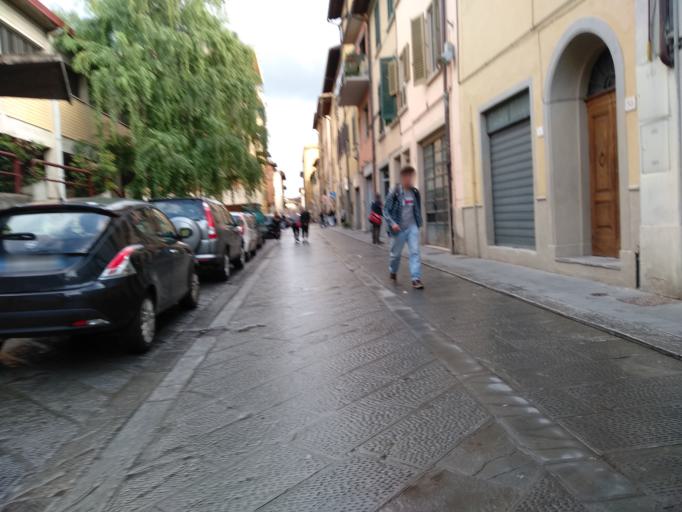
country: IT
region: Tuscany
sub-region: Province of Arezzo
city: San Giovanni Valdarno
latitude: 43.5664
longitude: 11.5297
